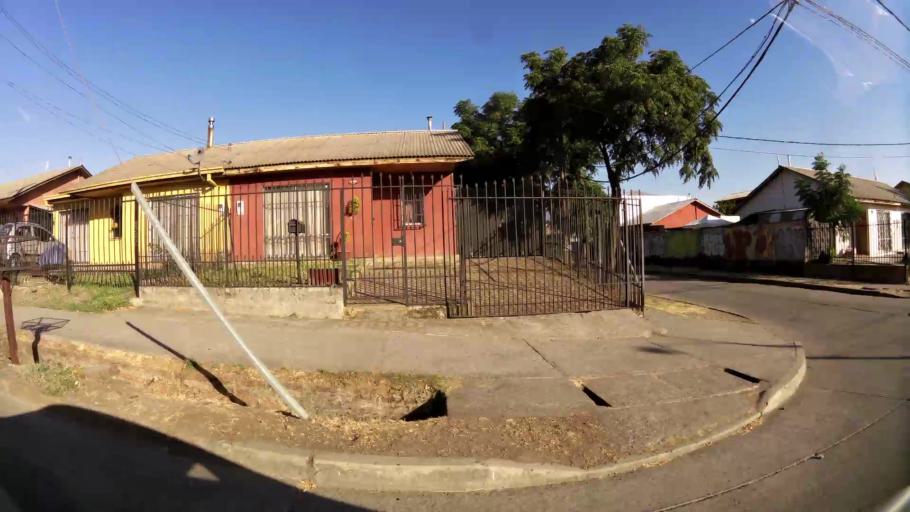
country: CL
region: Maule
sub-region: Provincia de Talca
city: Talca
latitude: -35.4384
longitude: -71.6916
